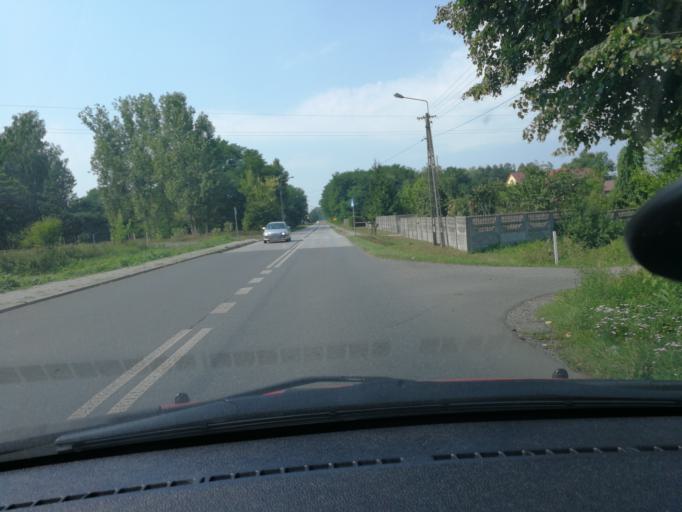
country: PL
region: Lodz Voivodeship
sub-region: powiat Lowicki
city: Bobrowniki
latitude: 52.0210
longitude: 20.0533
